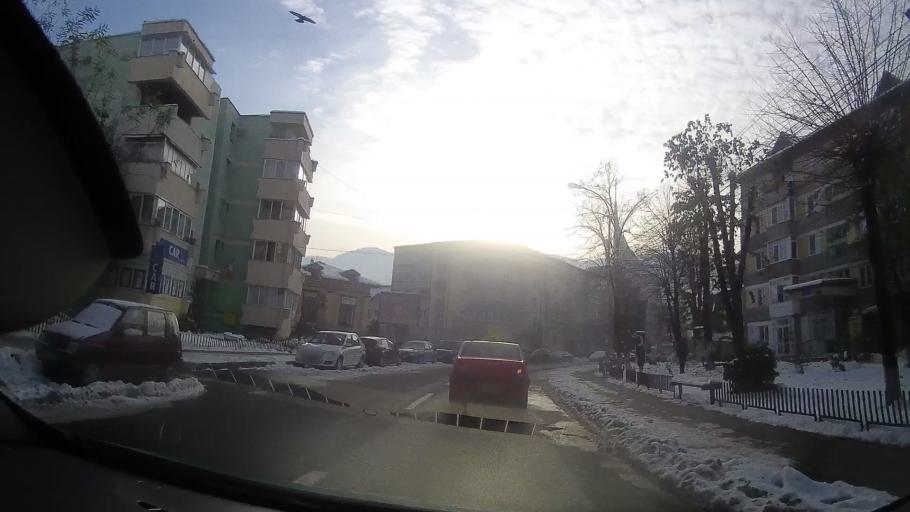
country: RO
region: Neamt
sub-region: Municipiul Piatra-Neamt
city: Valeni
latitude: 46.9272
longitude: 26.3694
